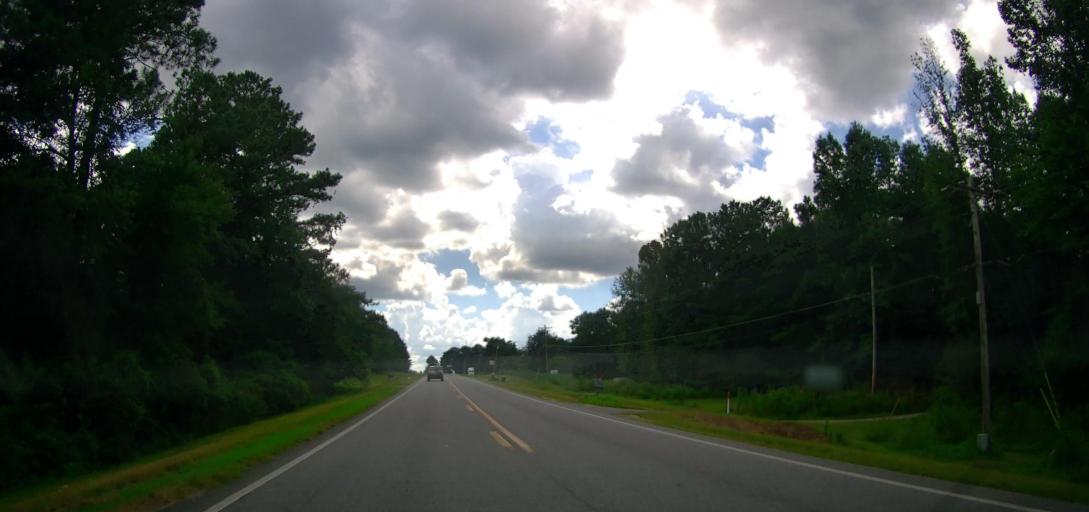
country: US
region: Alabama
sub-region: Russell County
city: Ladonia
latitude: 32.4507
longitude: -85.2275
